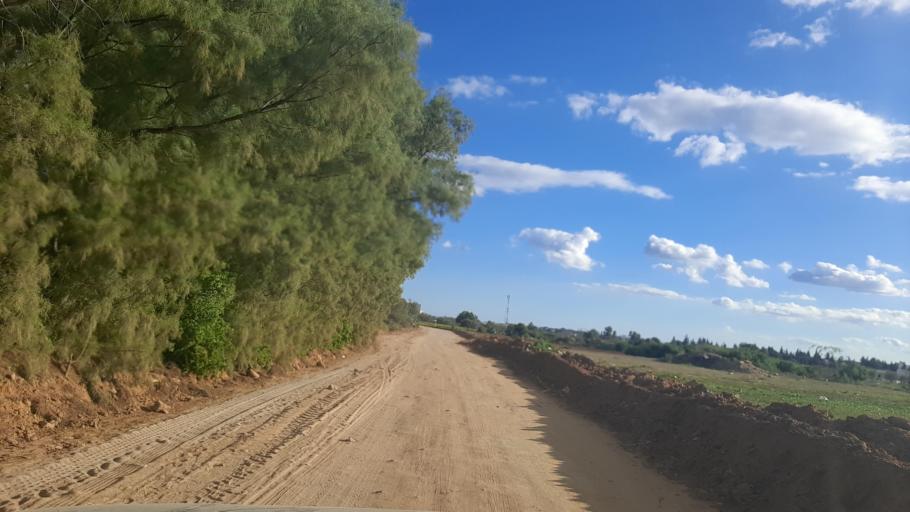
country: TN
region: Nabul
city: Al Hammamat
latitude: 36.4231
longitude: 10.5082
